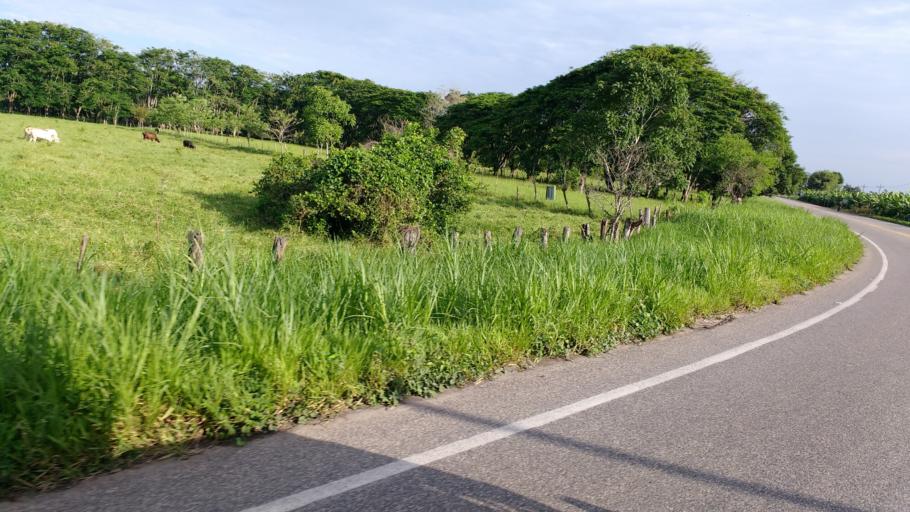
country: MX
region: Tabasco
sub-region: Teapa
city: Eureka y Belen
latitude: 17.6240
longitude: -92.9622
